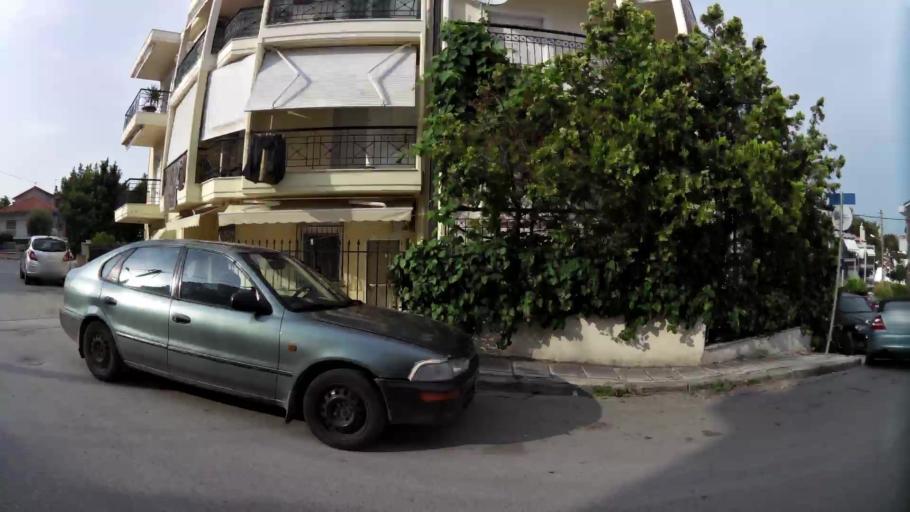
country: GR
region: Central Macedonia
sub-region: Nomos Thessalonikis
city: Oraiokastro
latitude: 40.7251
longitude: 22.9133
